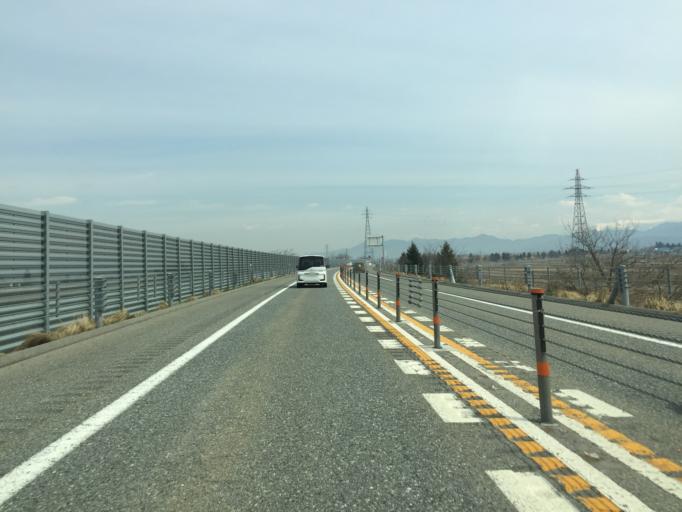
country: JP
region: Yamagata
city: Yonezawa
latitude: 37.9657
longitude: 140.1220
